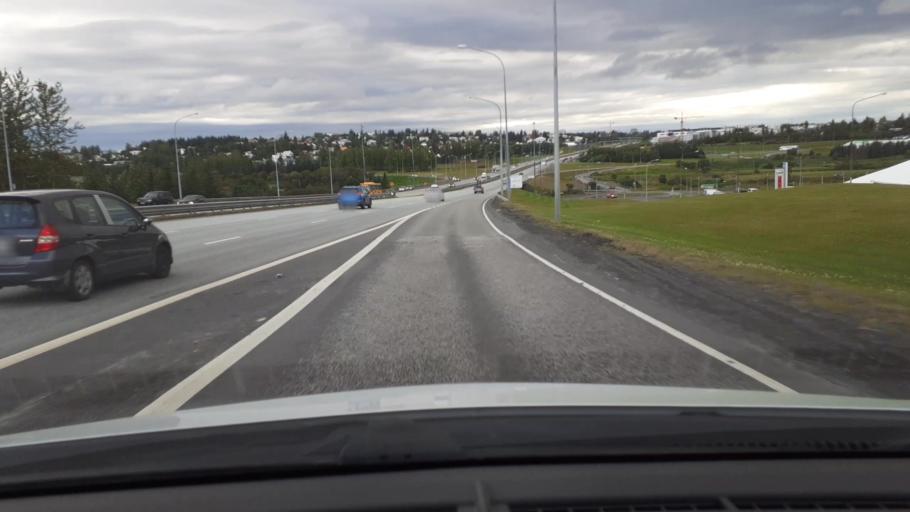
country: IS
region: Capital Region
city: Reykjavik
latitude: 64.1241
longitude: -21.8351
